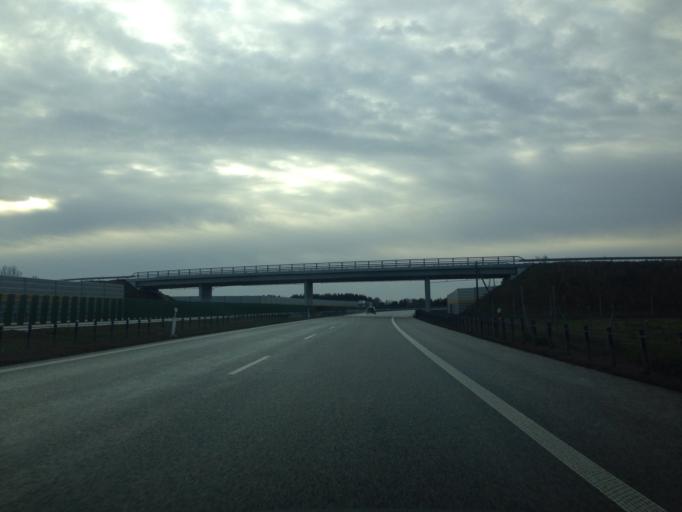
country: PL
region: Kujawsko-Pomorskie
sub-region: Powiat torunski
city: Lubicz Dolny
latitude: 52.9886
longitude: 18.7355
